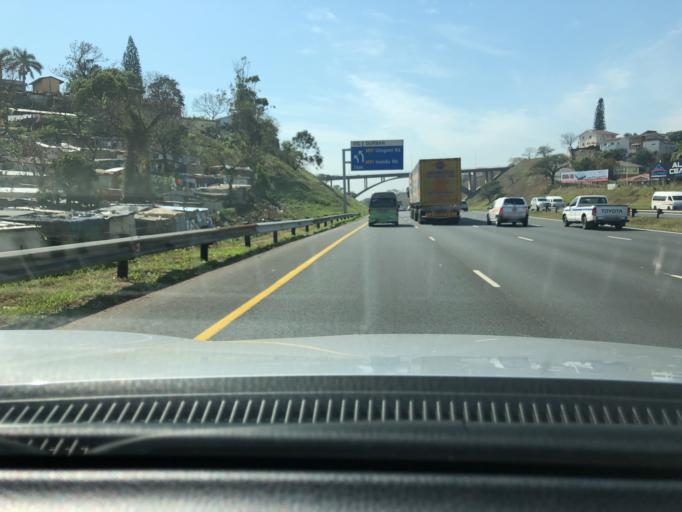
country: ZA
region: KwaZulu-Natal
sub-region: eThekwini Metropolitan Municipality
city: Berea
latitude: -29.8196
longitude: 30.9688
